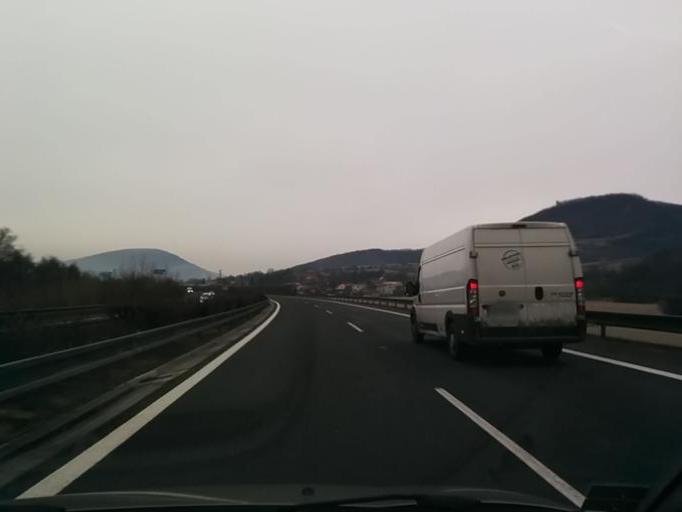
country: SK
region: Banskobystricky
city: Nova Bana
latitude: 48.3744
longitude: 18.6058
